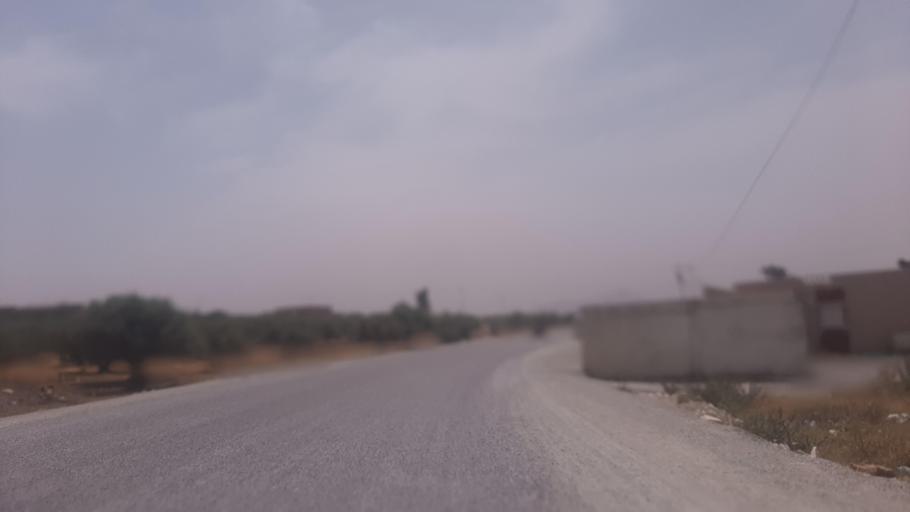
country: TN
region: Zaghwan
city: Zaghouan
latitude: 36.5268
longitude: 10.1591
